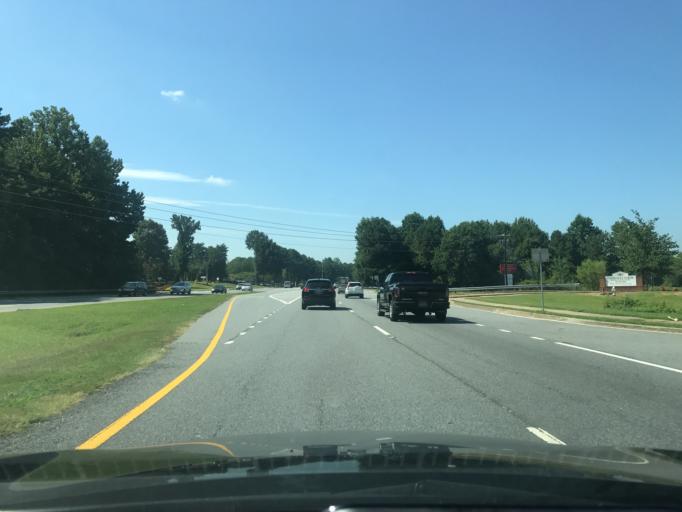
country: US
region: Georgia
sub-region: Gwinnett County
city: Norcross
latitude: 33.9666
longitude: -84.2230
